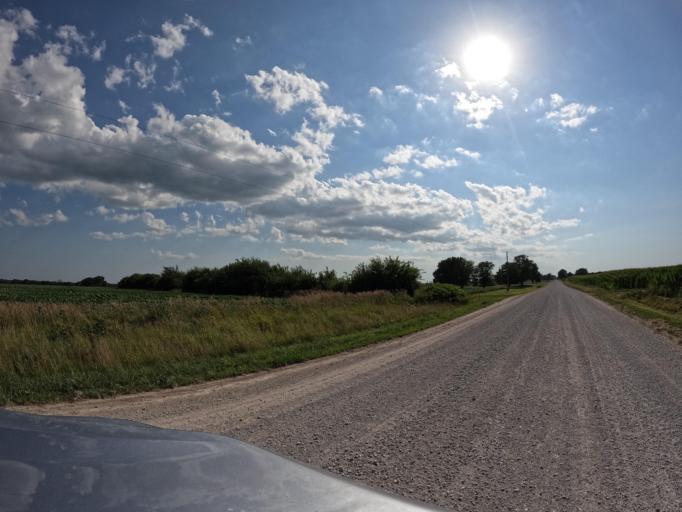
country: US
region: Iowa
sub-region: Appanoose County
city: Centerville
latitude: 40.7179
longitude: -93.0106
